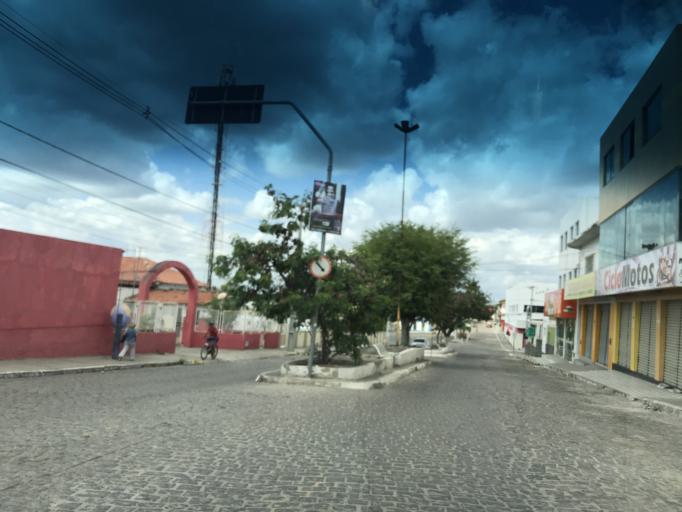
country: BR
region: Bahia
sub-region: Itaberaba
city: Itaberaba
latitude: -12.5313
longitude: -40.3059
